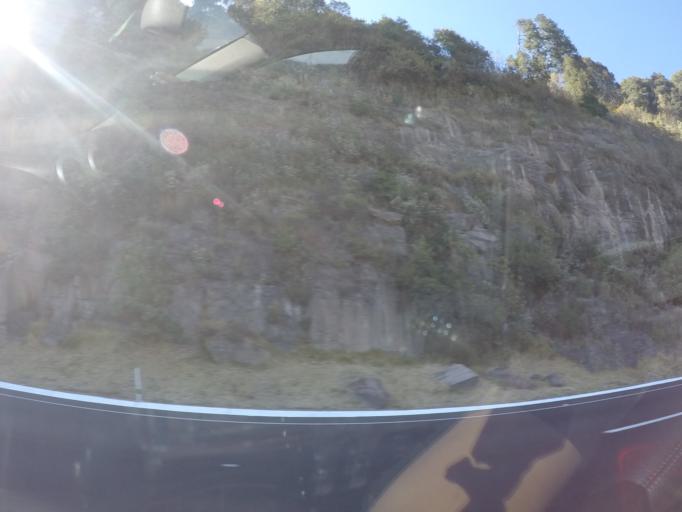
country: MX
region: Mexico City
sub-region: Cuajimalpa de Morelos
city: San Lorenzo Acopilco
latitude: 19.3137
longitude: -99.3395
